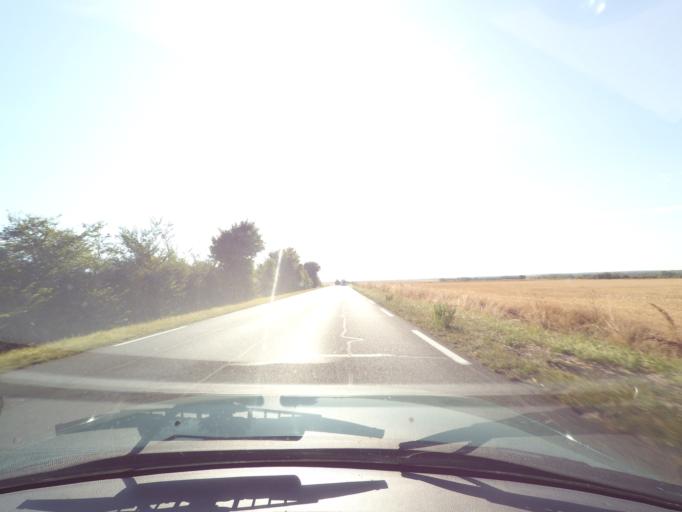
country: FR
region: Poitou-Charentes
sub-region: Departement de la Vienne
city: Ayron
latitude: 46.6557
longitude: 0.1051
